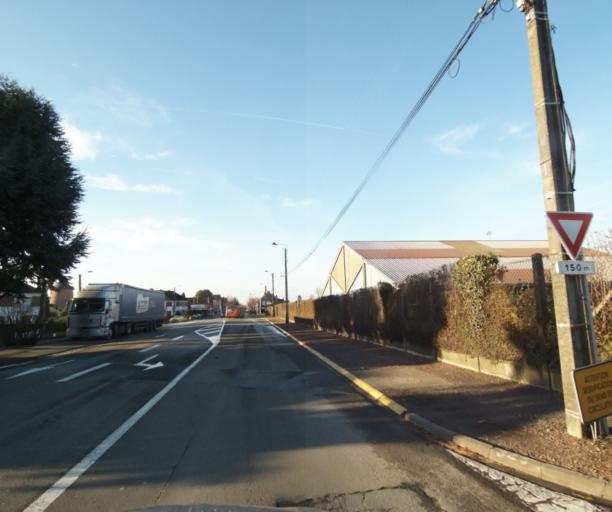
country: FR
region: Nord-Pas-de-Calais
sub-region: Departement du Nord
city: Marly
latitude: 50.3470
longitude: 3.5517
